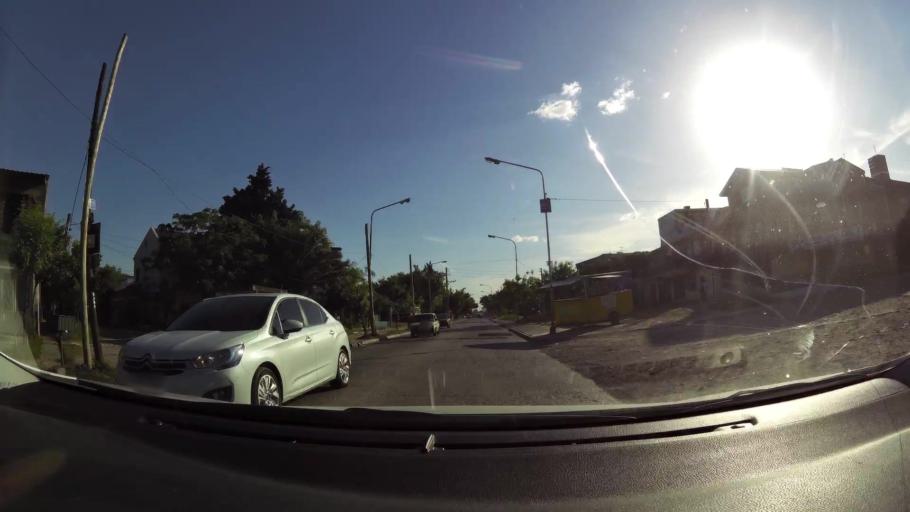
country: AR
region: Buenos Aires F.D.
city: Villa Lugano
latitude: -34.7000
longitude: -58.4717
